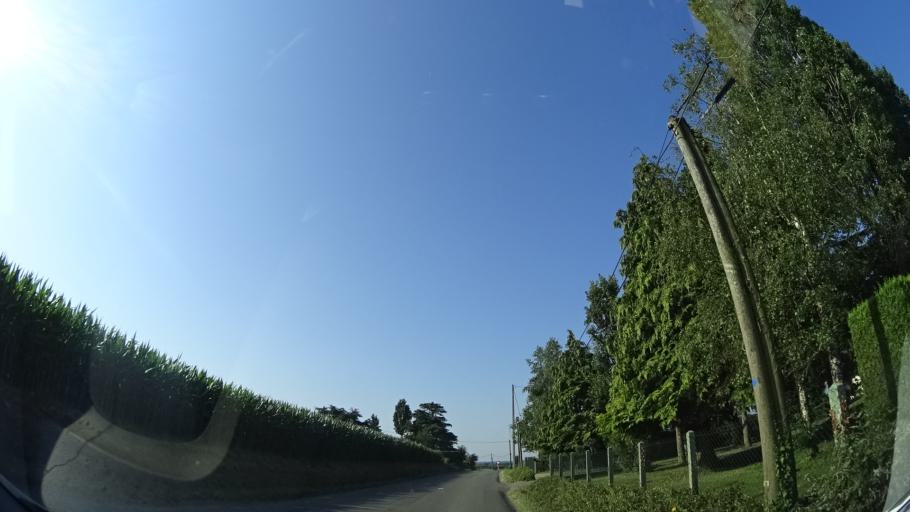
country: FR
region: Brittany
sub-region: Departement d'Ille-et-Vilaine
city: Pace
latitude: 48.1724
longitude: -1.7884
